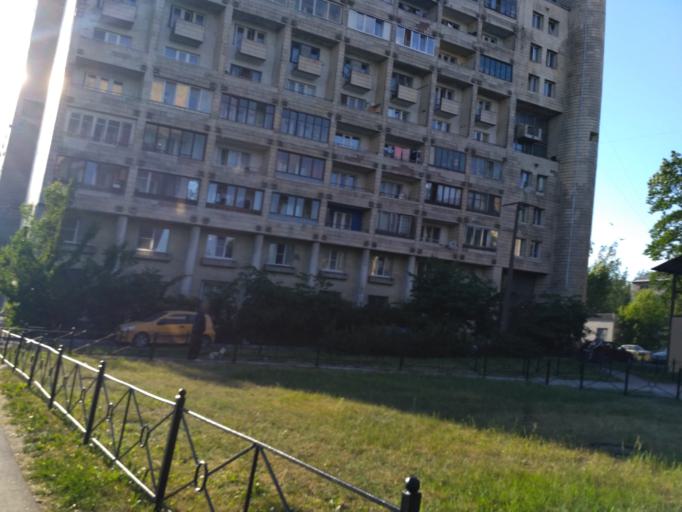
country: RU
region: St.-Petersburg
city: Kushelevka
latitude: 59.9975
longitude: 30.3736
